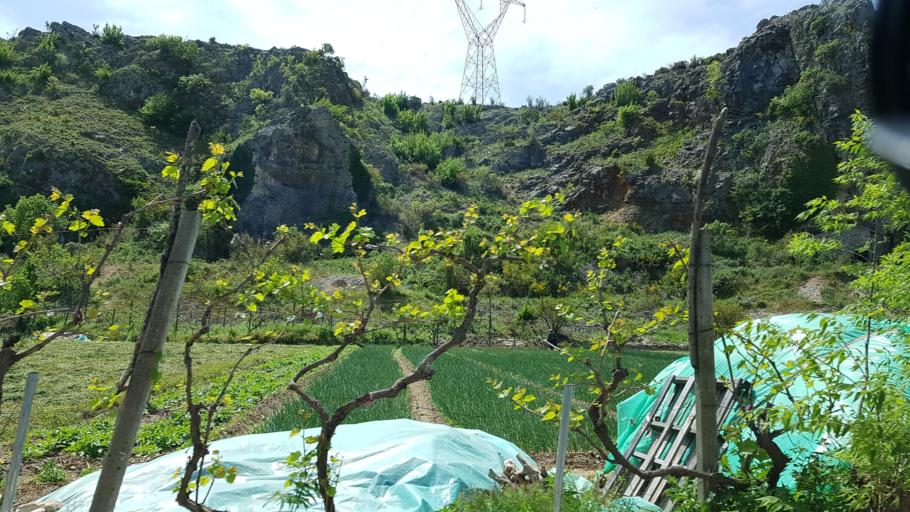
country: AL
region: Shkoder
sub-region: Rrethi i Malesia e Madhe
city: Gruemire
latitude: 42.1243
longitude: 19.5862
